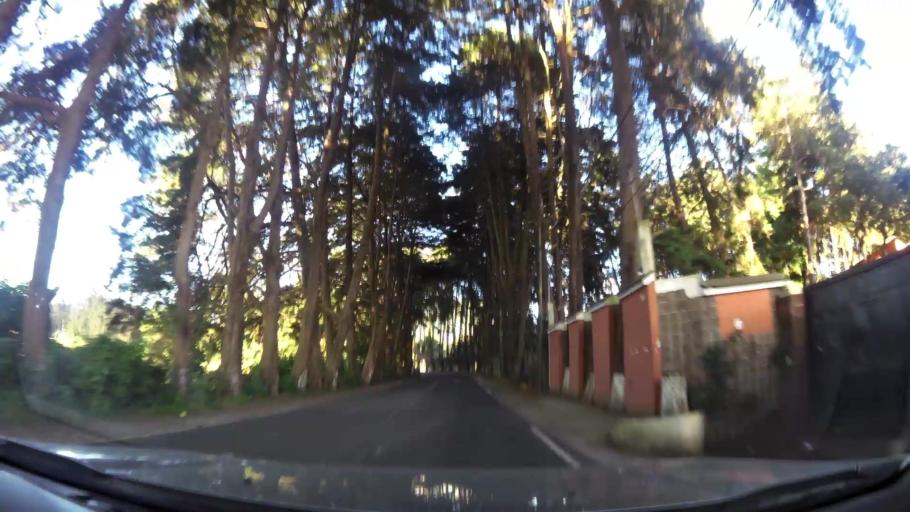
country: GT
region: Sacatepequez
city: San Lucas Sacatepequez
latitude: 14.6150
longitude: -90.6596
